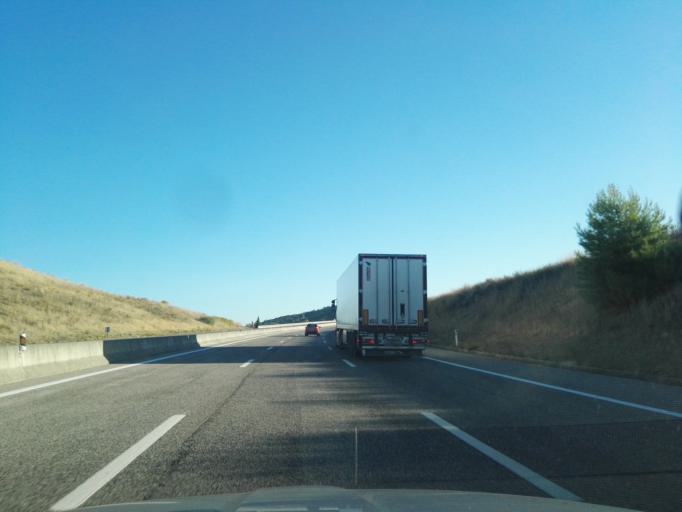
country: PT
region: Lisbon
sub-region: Vila Franca de Xira
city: Castanheira do Ribatejo
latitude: 39.0035
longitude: -9.0141
